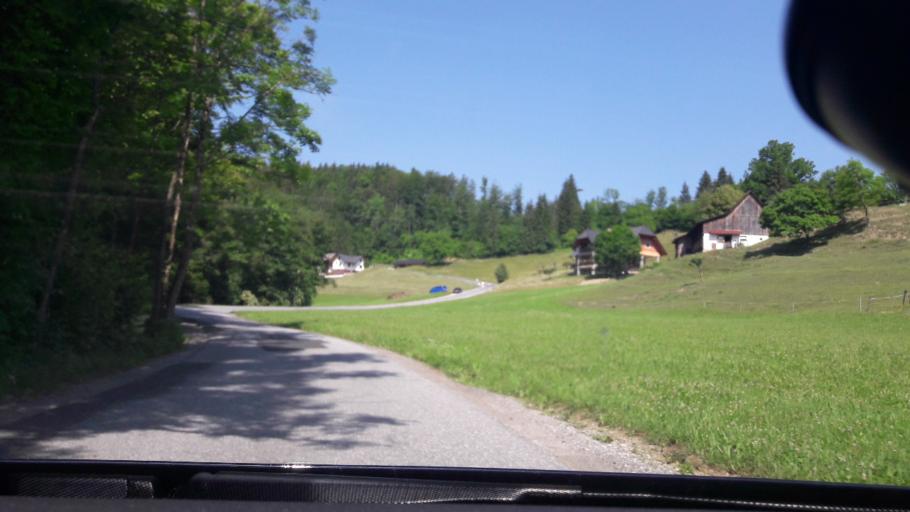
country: AT
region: Styria
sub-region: Politischer Bezirk Voitsberg
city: Sodingberg
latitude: 47.1106
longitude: 15.1619
